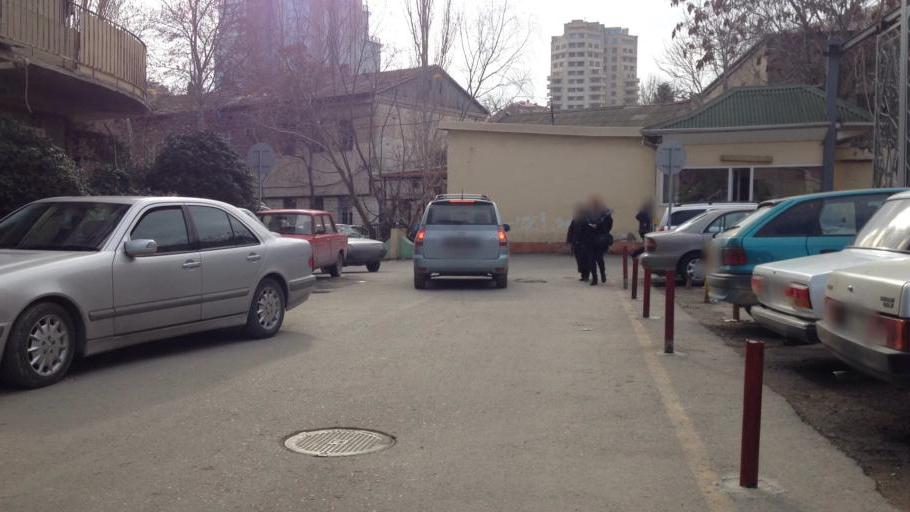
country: AZ
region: Baki
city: Baku
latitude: 40.3811
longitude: 49.8531
